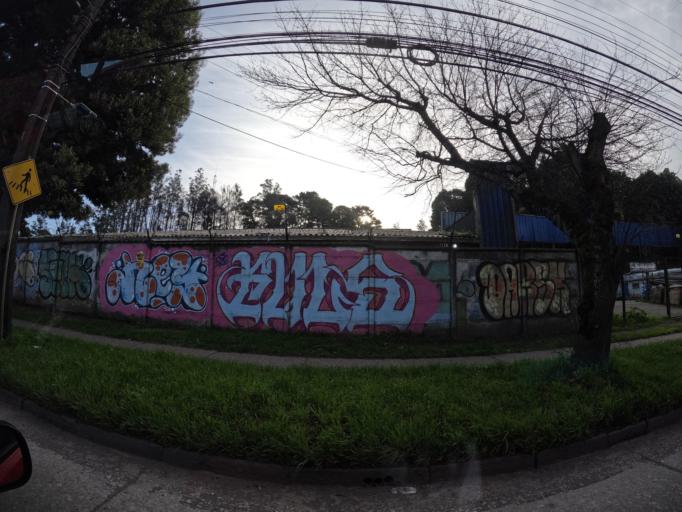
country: CL
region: Biobio
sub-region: Provincia de Concepcion
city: Concepcion
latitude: -36.8064
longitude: -73.0318
